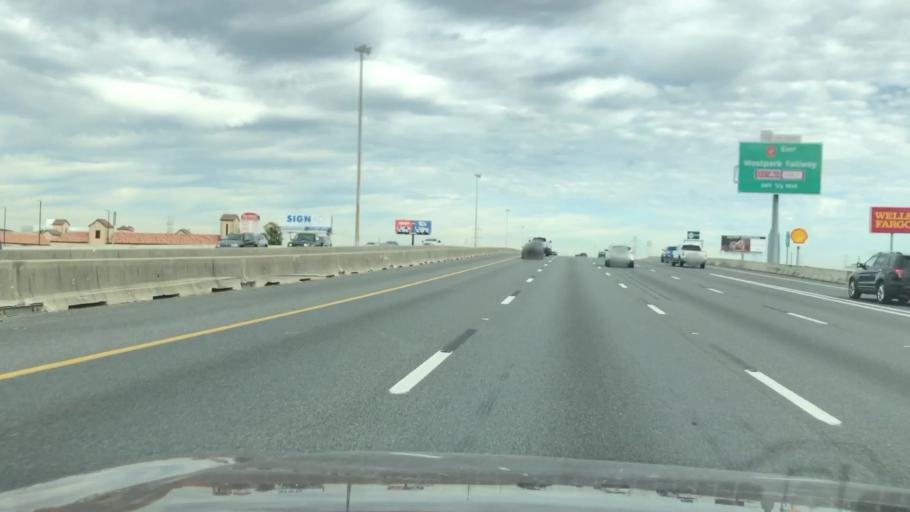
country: US
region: Texas
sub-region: Harris County
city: Bellaire
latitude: 29.7154
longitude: -95.5005
